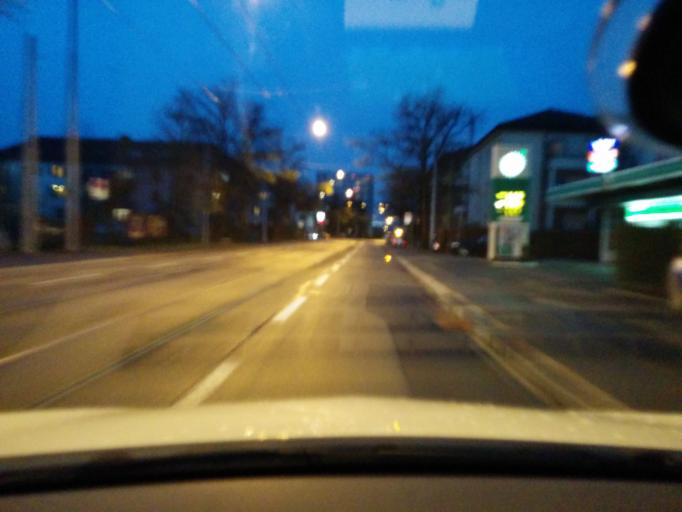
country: CH
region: Zurich
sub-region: Bezirk Zuerich
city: Zuerich (Kreis 11) / Oerlikon
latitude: 47.4065
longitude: 8.5381
